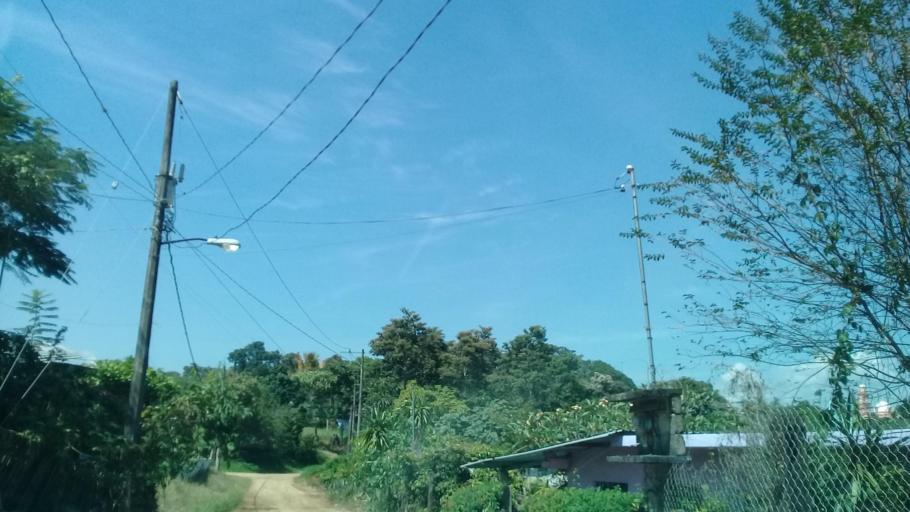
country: MX
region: Veracruz
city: Amatlan de los Reyes
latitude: 18.8379
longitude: -96.9138
